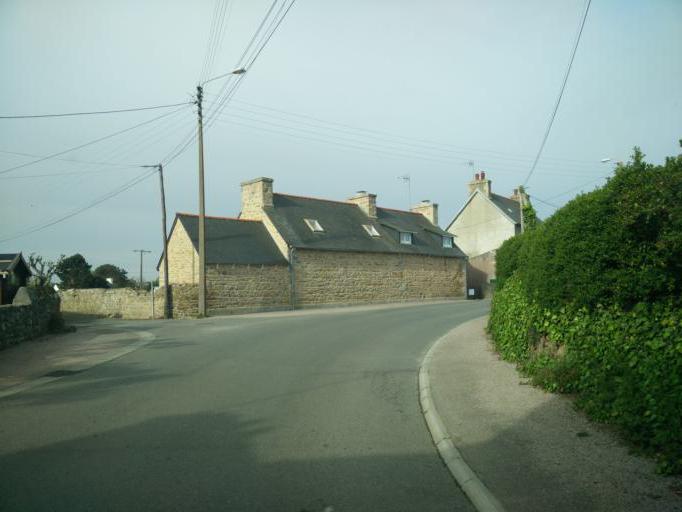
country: FR
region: Brittany
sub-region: Departement des Cotes-d'Armor
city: Pleubian
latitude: 48.8624
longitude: -3.0980
